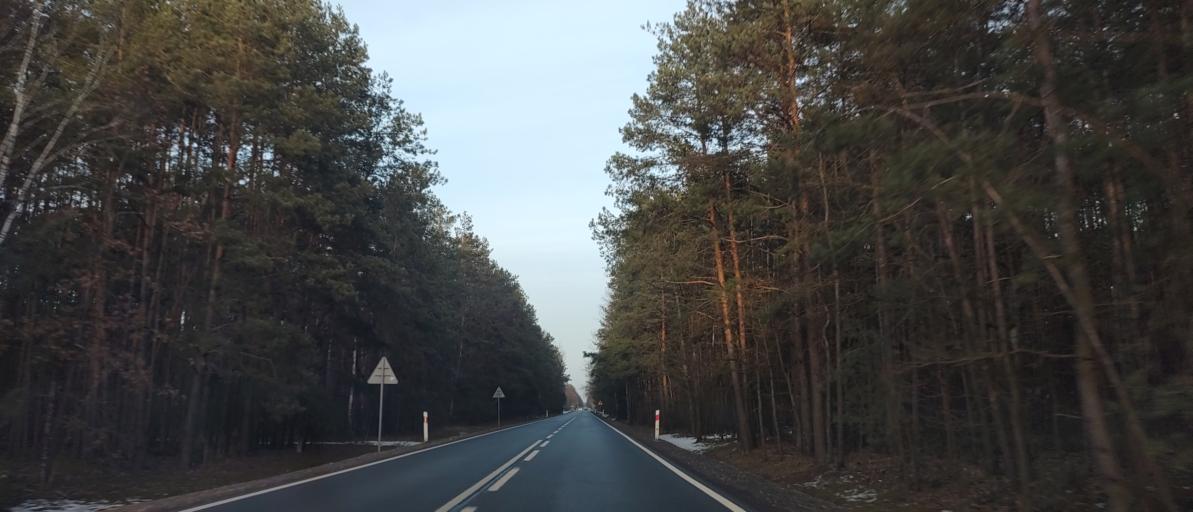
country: PL
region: Masovian Voivodeship
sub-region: Powiat bialobrzeski
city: Sucha
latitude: 51.6303
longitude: 20.8889
